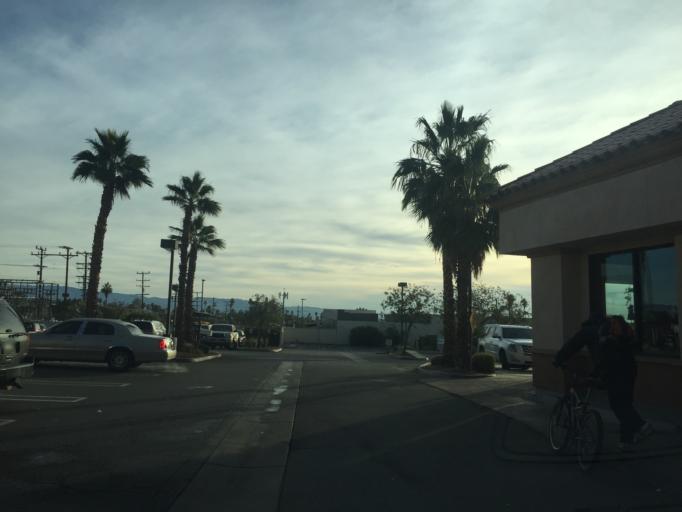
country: US
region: California
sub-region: Riverside County
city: Palm Springs
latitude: 33.8126
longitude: -116.5445
